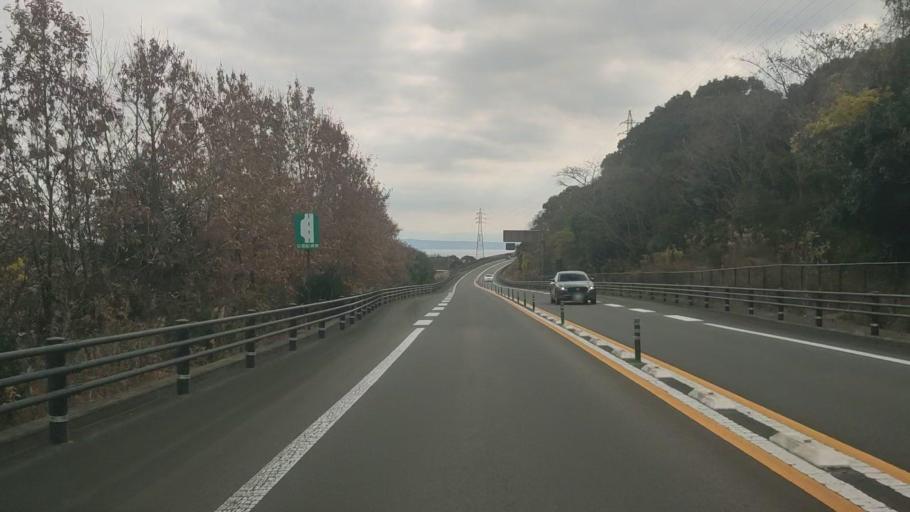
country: JP
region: Nagasaki
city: Shimabara
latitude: 32.7848
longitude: 130.3513
